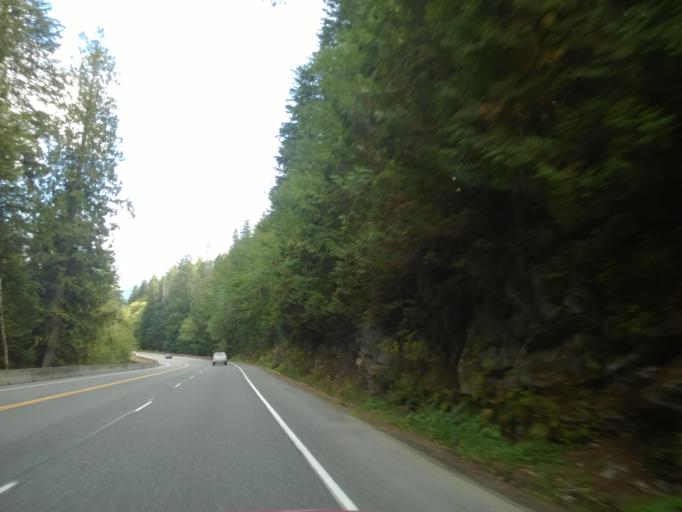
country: US
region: Washington
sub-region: Snohomish County
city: Gold Bar
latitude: 47.7164
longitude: -121.2118
